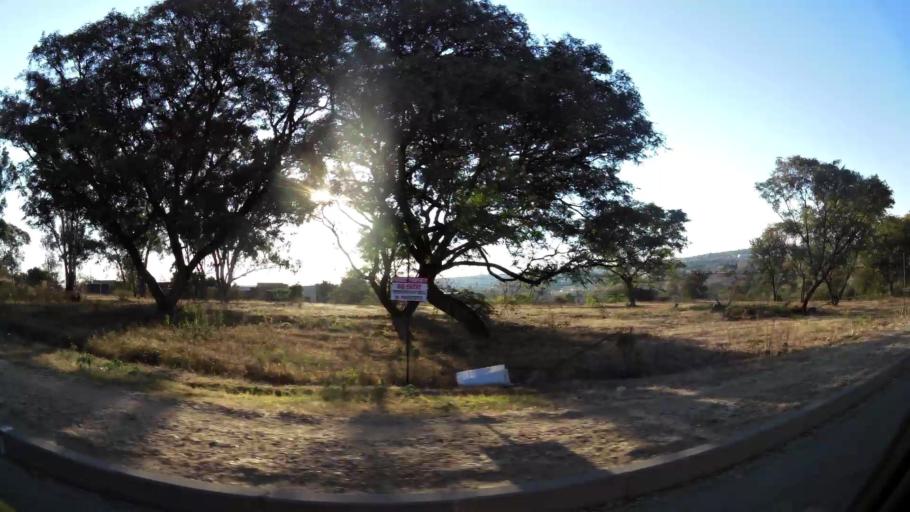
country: ZA
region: Gauteng
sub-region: City of Johannesburg Metropolitan Municipality
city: Midrand
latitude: -26.0049
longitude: 28.1178
